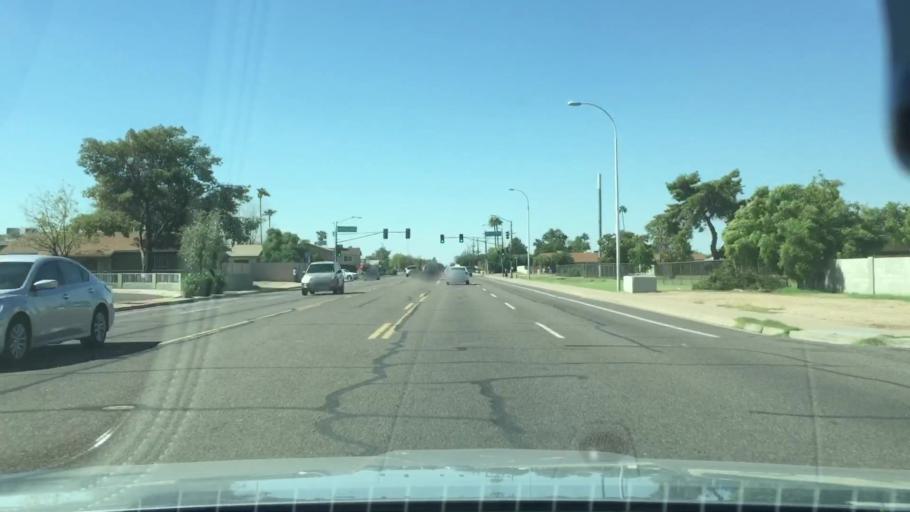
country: US
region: Arizona
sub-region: Maricopa County
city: Guadalupe
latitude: 33.3928
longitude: -111.9847
